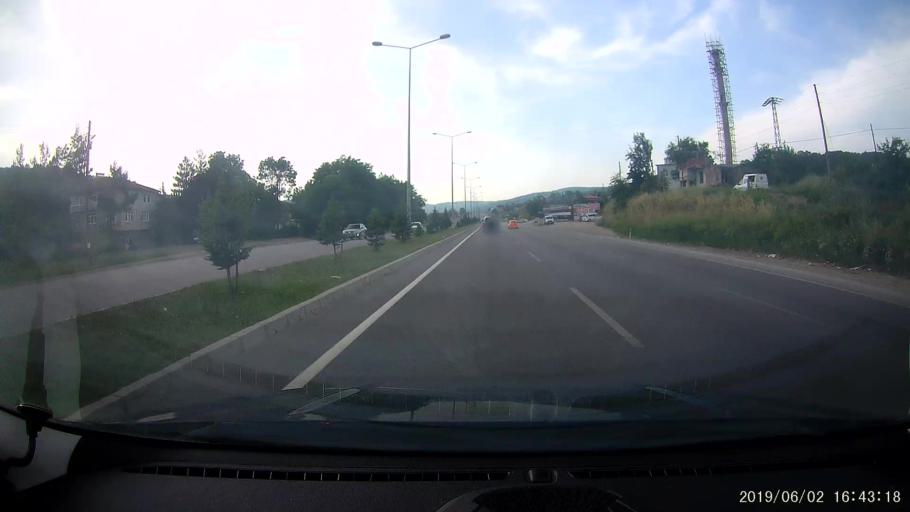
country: TR
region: Samsun
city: Kavak
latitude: 41.1331
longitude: 36.1299
